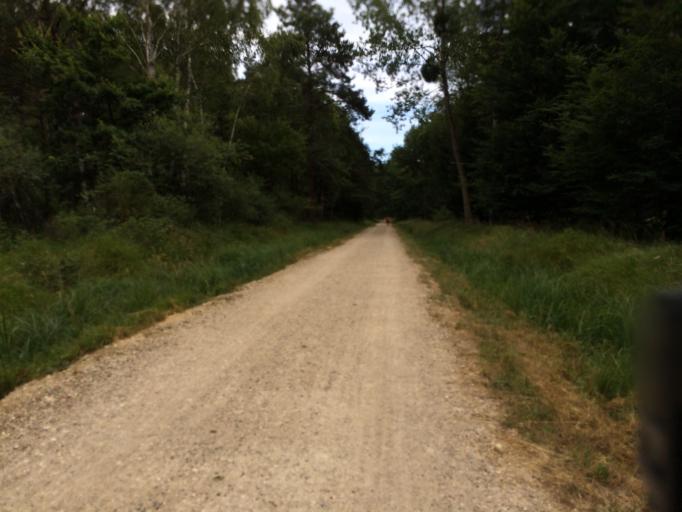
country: FR
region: Ile-de-France
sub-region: Departement de l'Essonne
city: Brunoy
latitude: 48.6762
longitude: 2.4799
